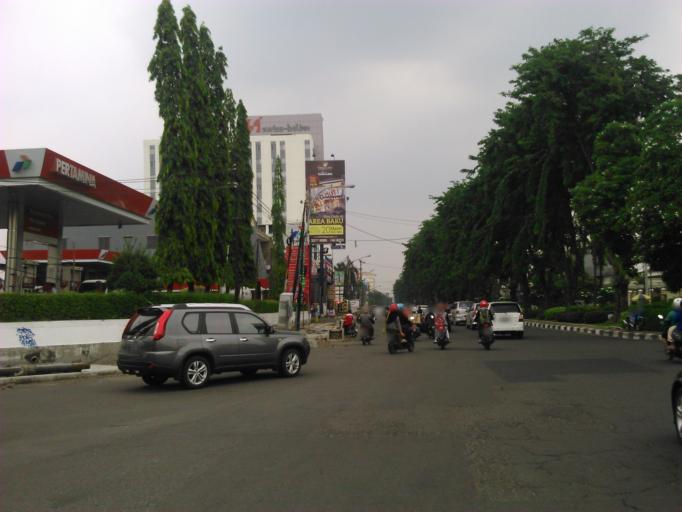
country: ID
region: East Java
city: Gubengairlangga
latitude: -7.2806
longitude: 112.7721
